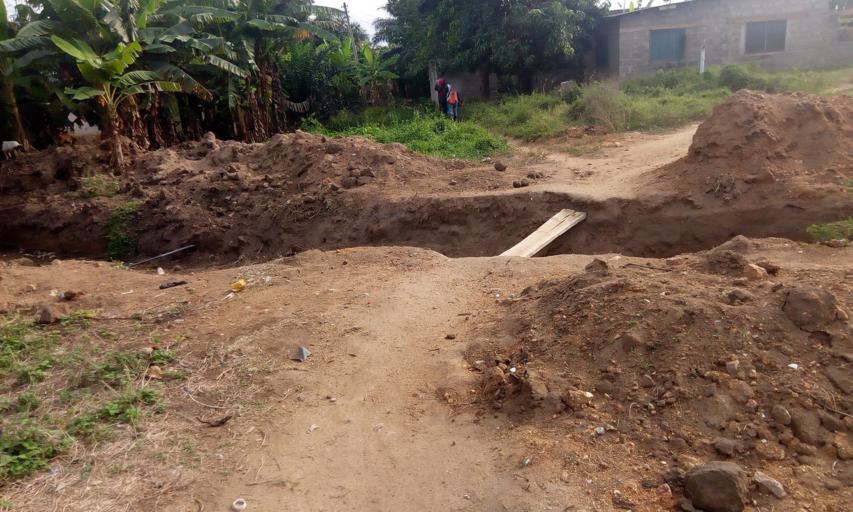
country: GH
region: Central
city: Winneba
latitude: 5.3556
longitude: -0.6266
